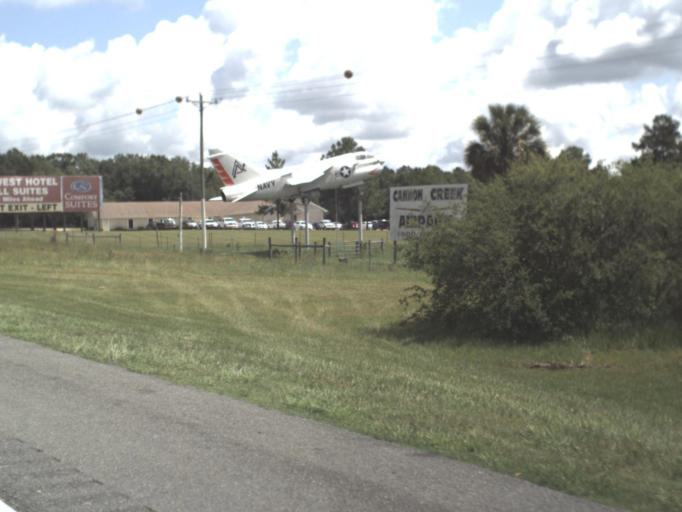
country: US
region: Florida
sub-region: Columbia County
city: Lake City
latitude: 30.1498
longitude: -82.6731
